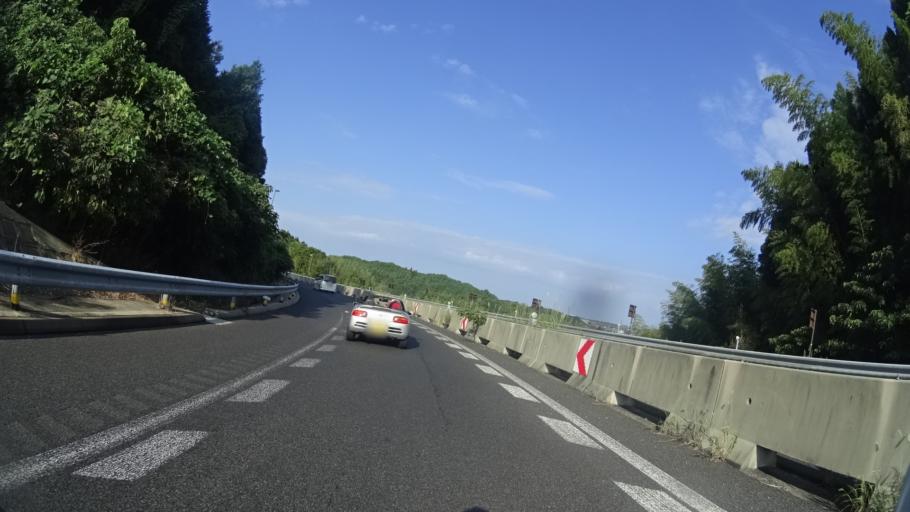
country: JP
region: Shimane
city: Izumo
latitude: 35.3271
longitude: 132.7154
